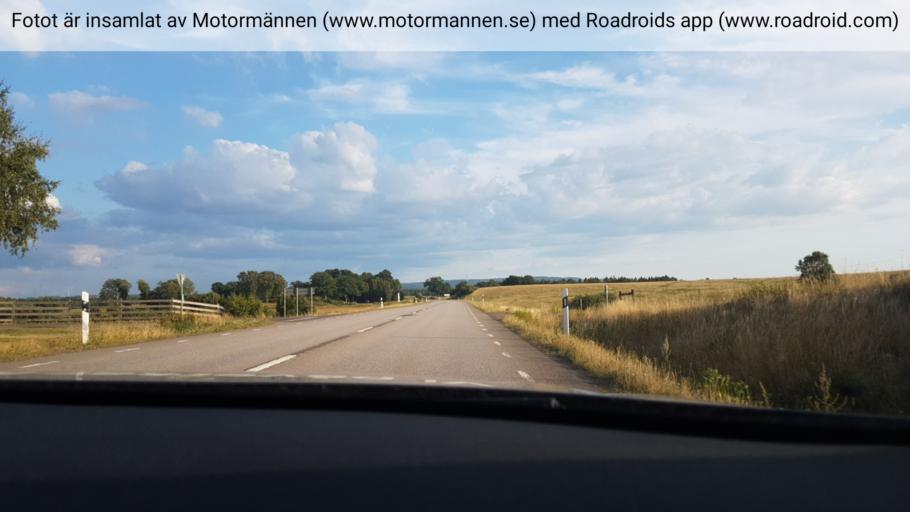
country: SE
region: Vaestra Goetaland
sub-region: Skara Kommun
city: Skara
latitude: 58.2816
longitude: 13.4844
